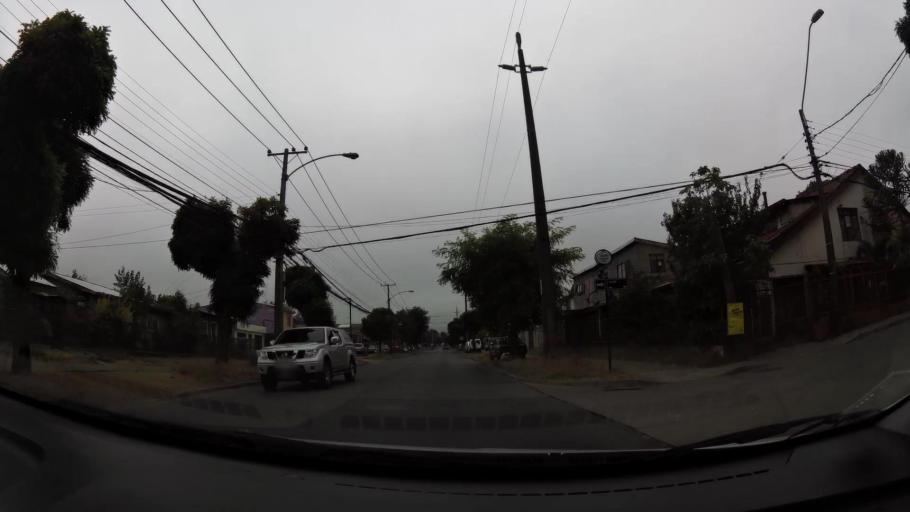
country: CL
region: Biobio
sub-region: Provincia de Concepcion
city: Concepcion
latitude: -36.8159
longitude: -73.0430
